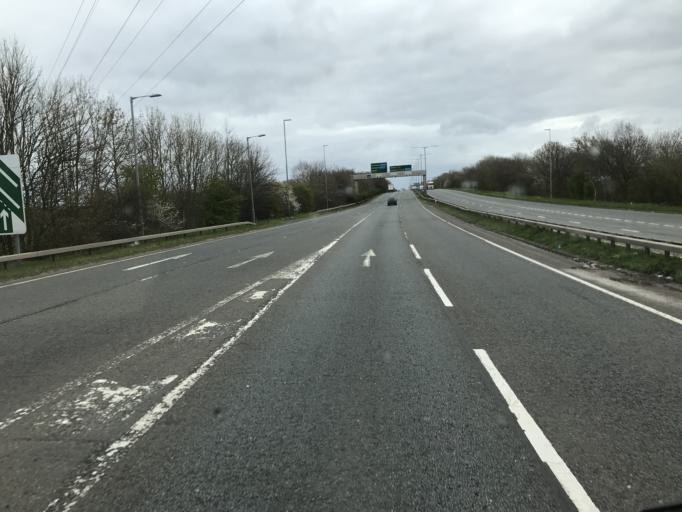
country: GB
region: England
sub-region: Borough of Halton
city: Hale
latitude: 53.3575
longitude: -2.8035
